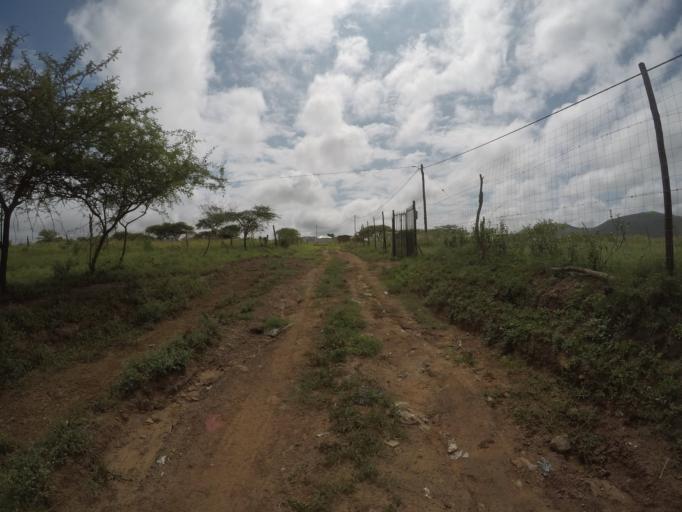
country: ZA
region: KwaZulu-Natal
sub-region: uThungulu District Municipality
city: Empangeni
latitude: -28.5837
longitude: 31.8490
